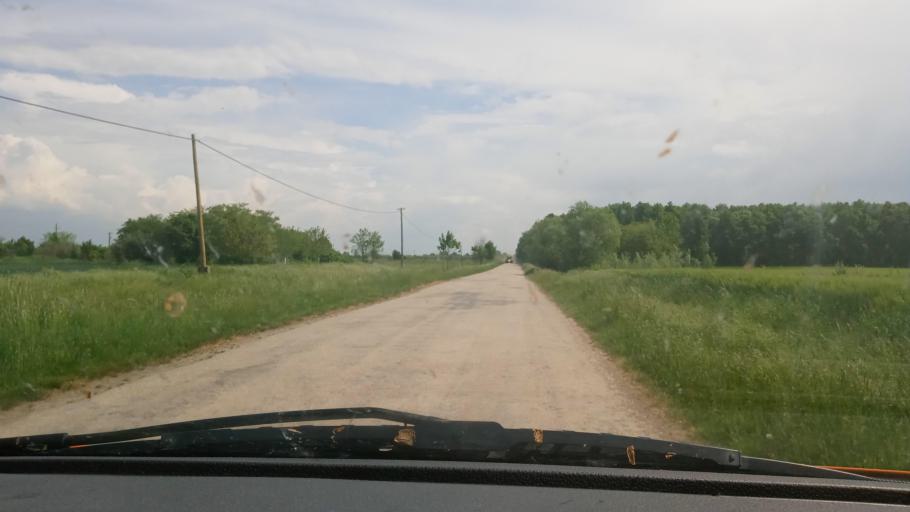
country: HU
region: Baranya
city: Siklos
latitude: 45.8066
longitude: 18.3432
